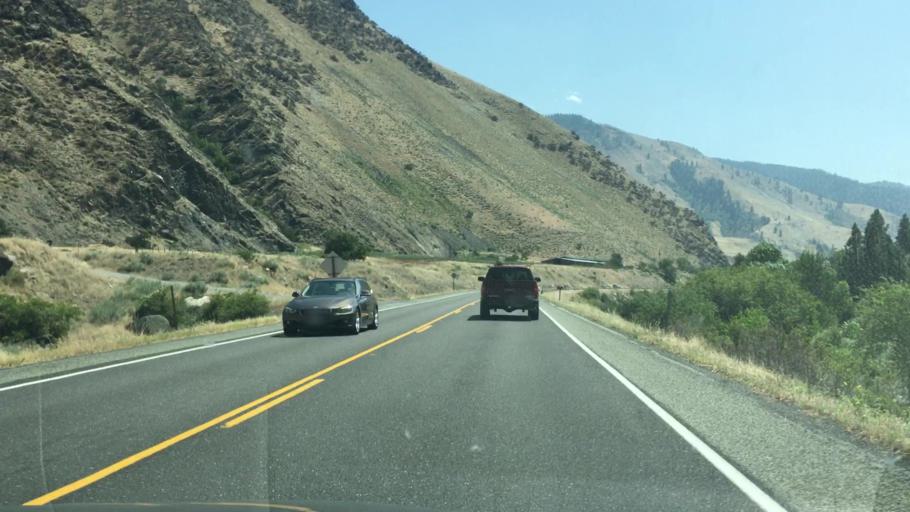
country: US
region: Idaho
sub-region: Valley County
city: McCall
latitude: 45.3544
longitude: -116.3586
